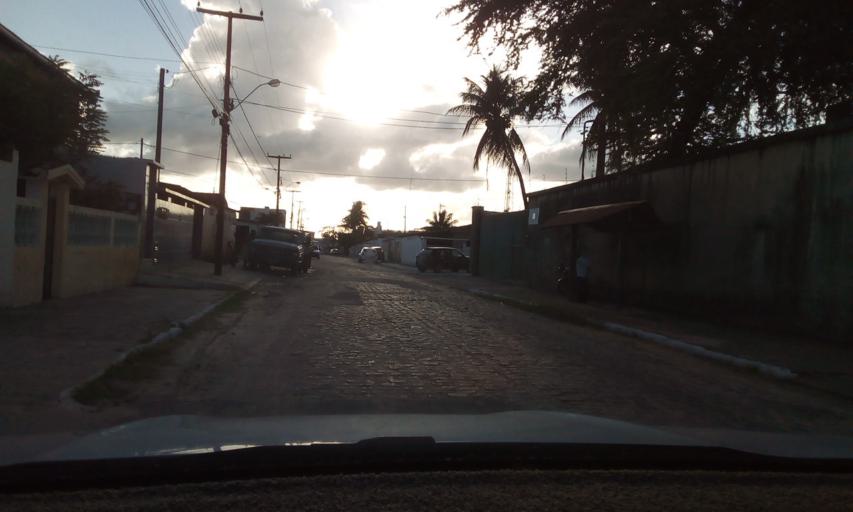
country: BR
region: Paraiba
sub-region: Bayeux
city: Bayeux
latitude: -7.1726
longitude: -34.8918
